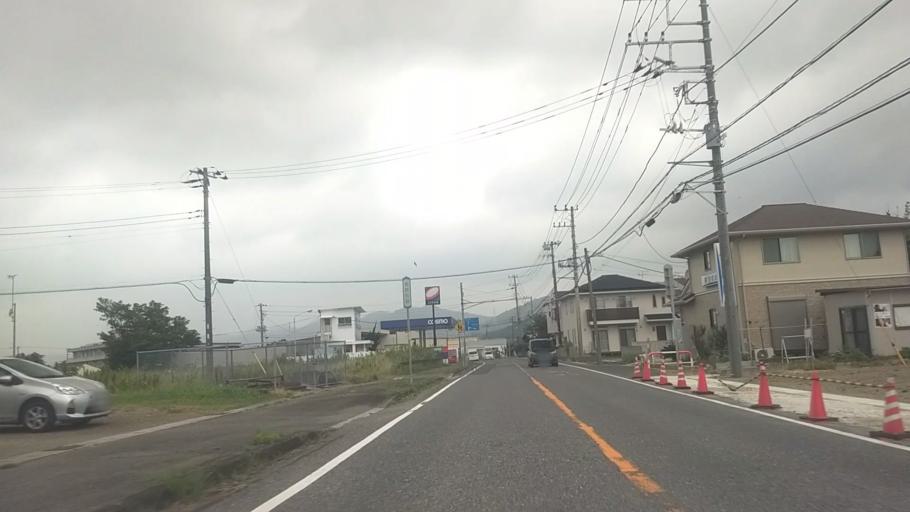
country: JP
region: Chiba
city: Kawaguchi
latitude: 35.1198
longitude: 140.0710
